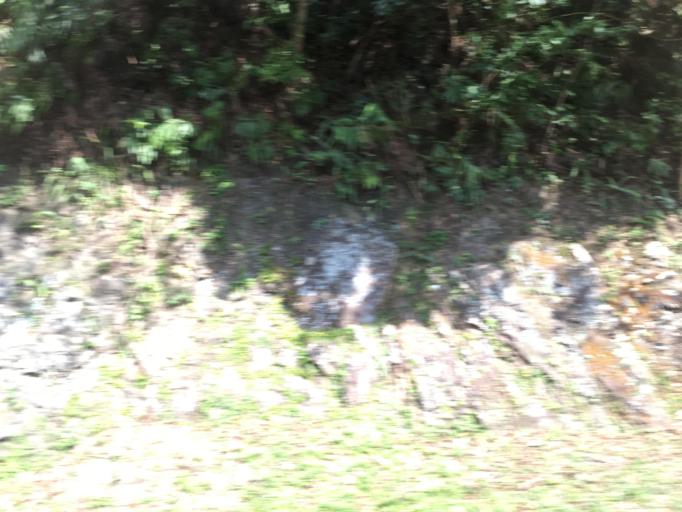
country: TW
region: Taiwan
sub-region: Yilan
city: Yilan
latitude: 24.6283
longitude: 121.5444
